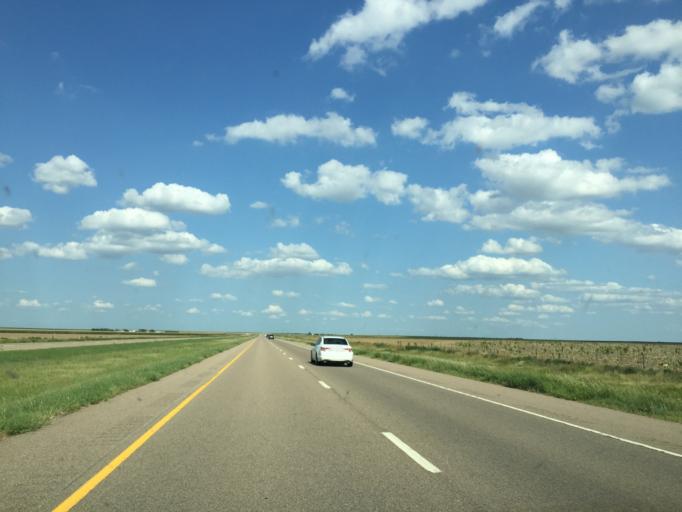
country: US
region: Kansas
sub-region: Gove County
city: Gove
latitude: 39.0973
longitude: -100.3485
